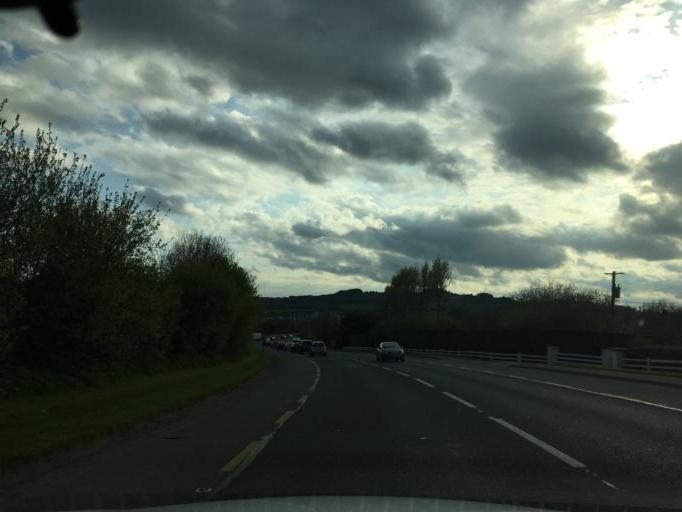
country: IE
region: Leinster
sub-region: Loch Garman
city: Loch Garman
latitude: 52.3402
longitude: -6.5083
